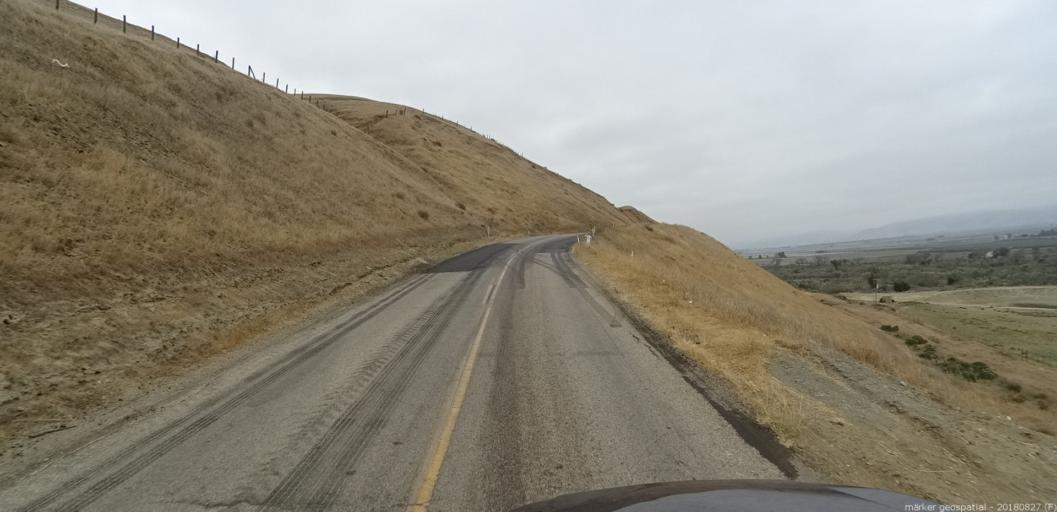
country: US
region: California
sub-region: Monterey County
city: Greenfield
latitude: 36.3231
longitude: -121.1826
